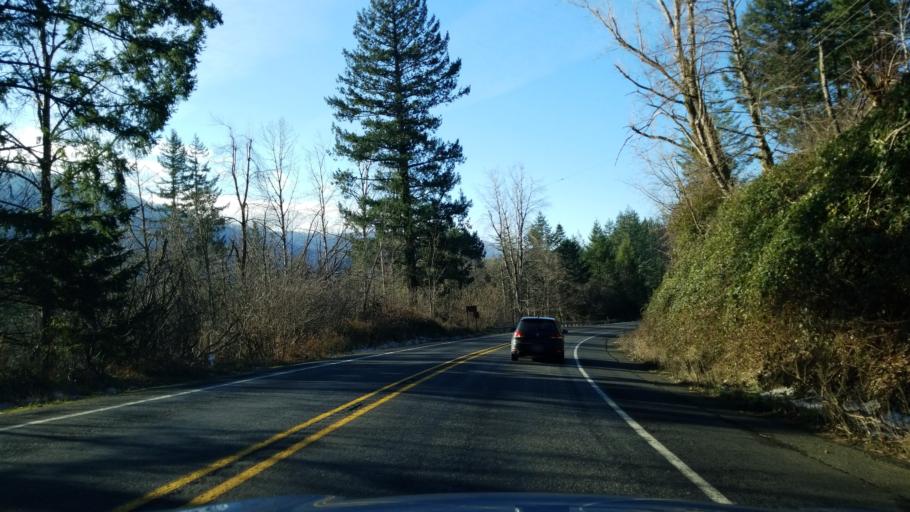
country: US
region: Oregon
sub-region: Hood River County
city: Cascade Locks
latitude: 45.6226
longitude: -122.0261
